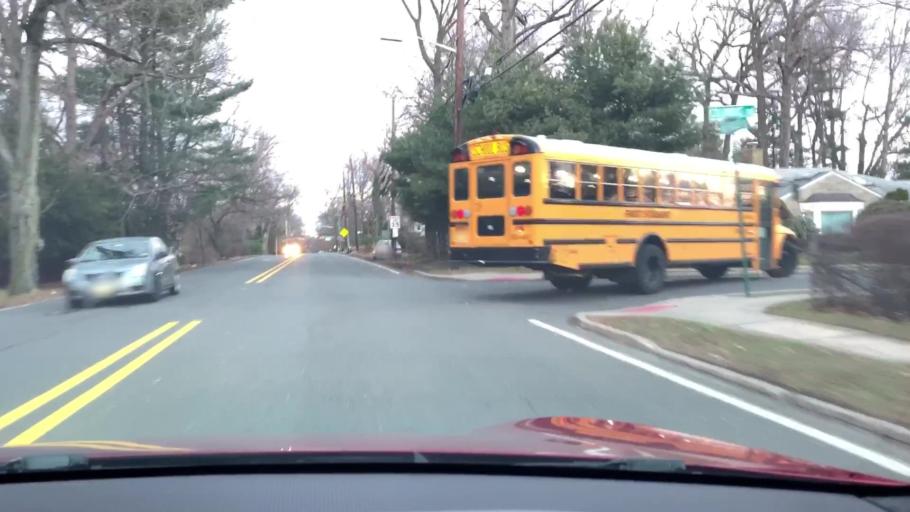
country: US
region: New Jersey
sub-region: Bergen County
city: Tenafly
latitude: 40.9310
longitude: -73.9776
